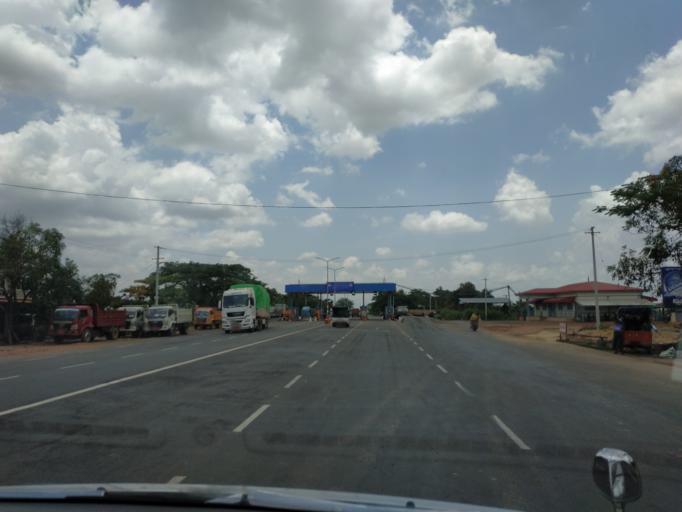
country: MM
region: Bago
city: Bago
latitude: 17.4716
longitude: 96.5457
